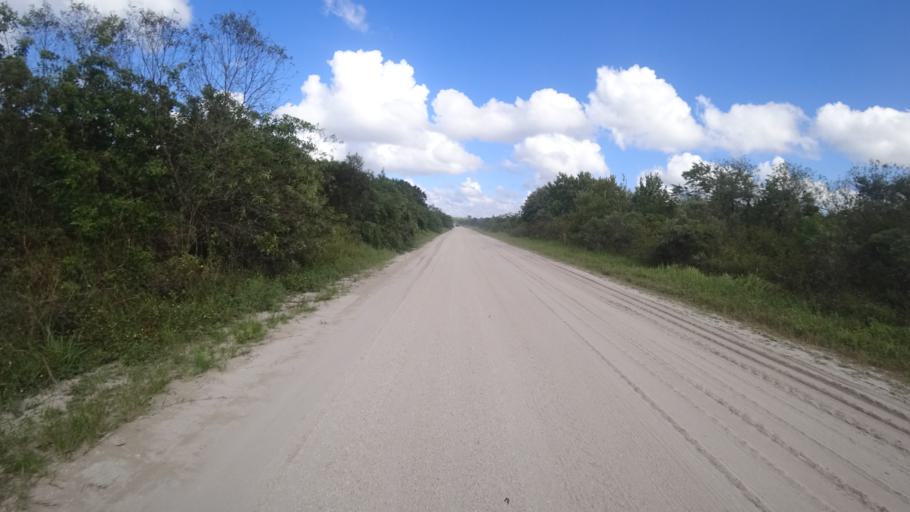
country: US
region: Florida
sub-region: Hillsborough County
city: Wimauma
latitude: 27.4429
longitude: -82.1826
